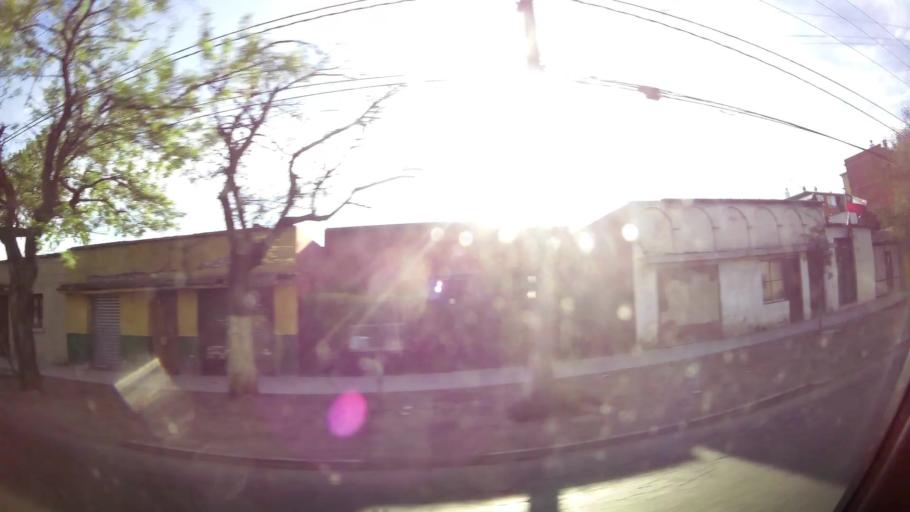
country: CL
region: Santiago Metropolitan
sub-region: Provincia de Santiago
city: Lo Prado
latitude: -33.4390
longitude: -70.7072
